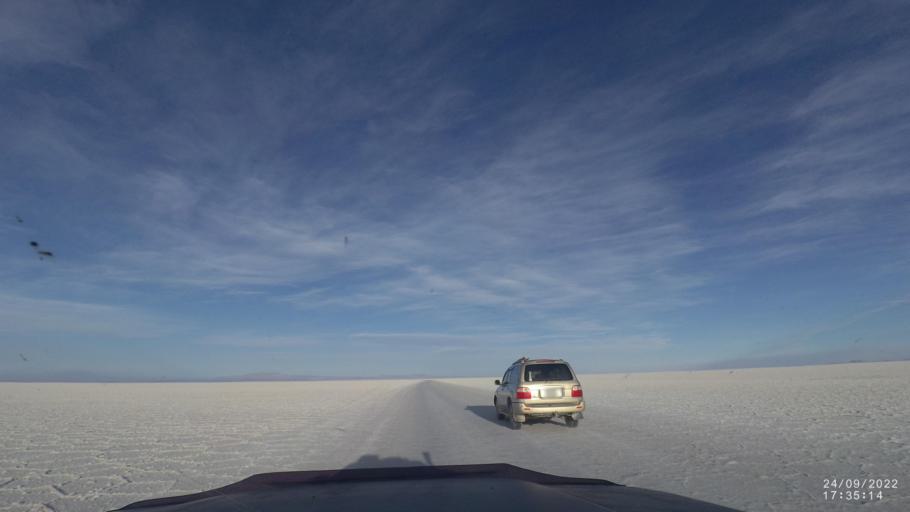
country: BO
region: Potosi
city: Colchani
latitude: -20.3231
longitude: -67.2623
